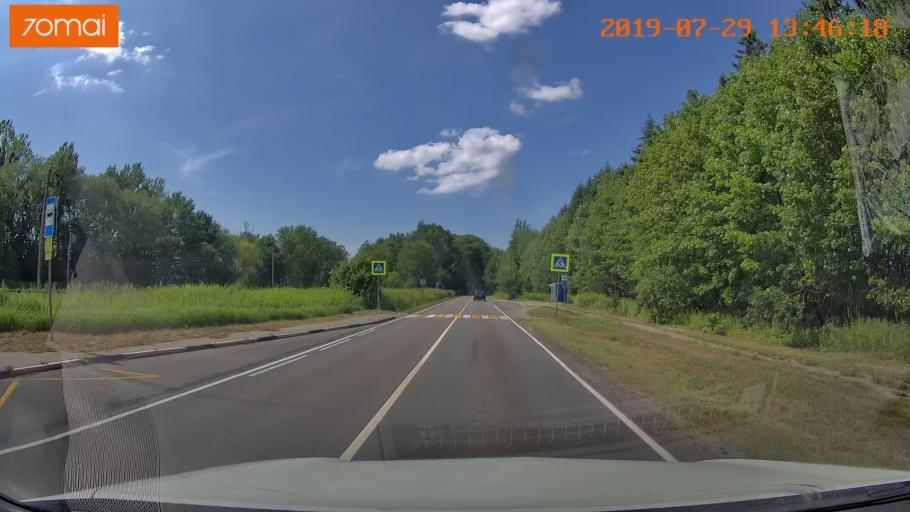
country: RU
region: Kaliningrad
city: Primorsk
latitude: 54.7403
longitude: 20.0666
